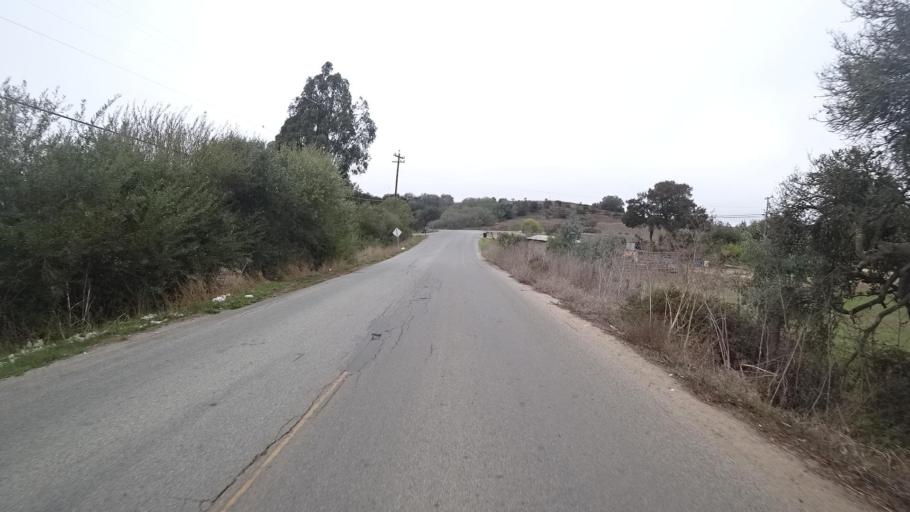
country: US
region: California
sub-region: Monterey County
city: Las Lomas
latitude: 36.8603
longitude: -121.7076
